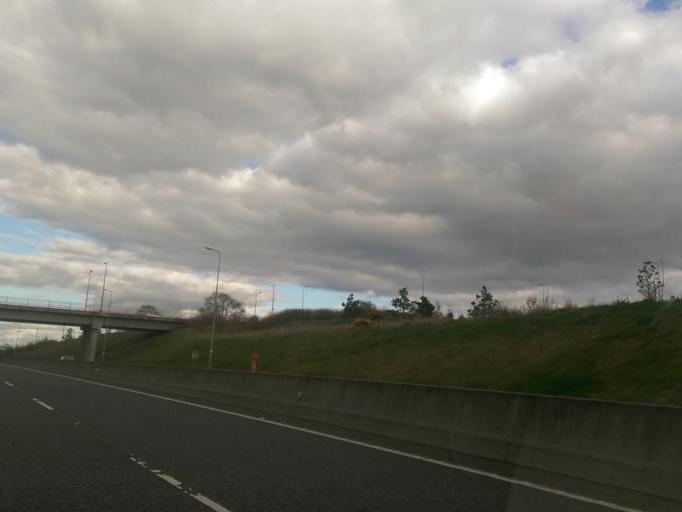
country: IE
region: Leinster
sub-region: An Iarmhi
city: Moate
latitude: 53.3866
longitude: -7.6849
